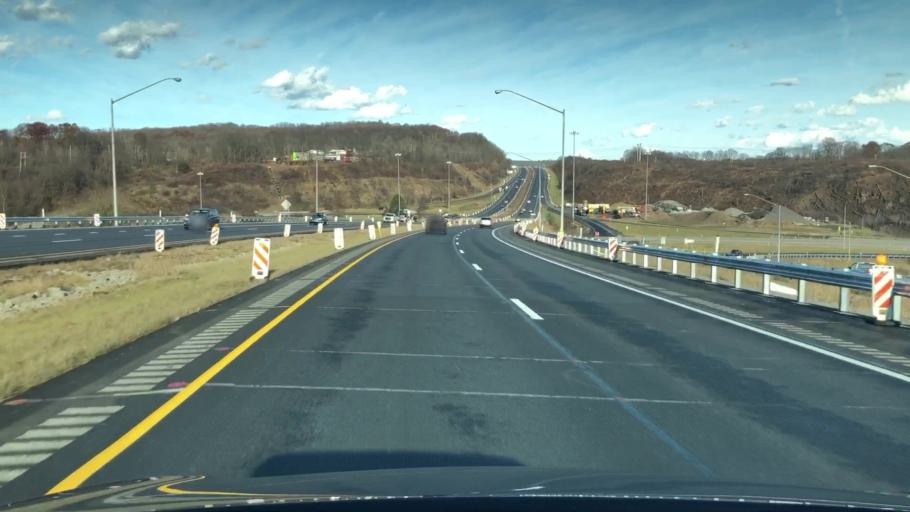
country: US
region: Pennsylvania
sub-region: Allegheny County
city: Tarentum
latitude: 40.6114
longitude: -79.7601
